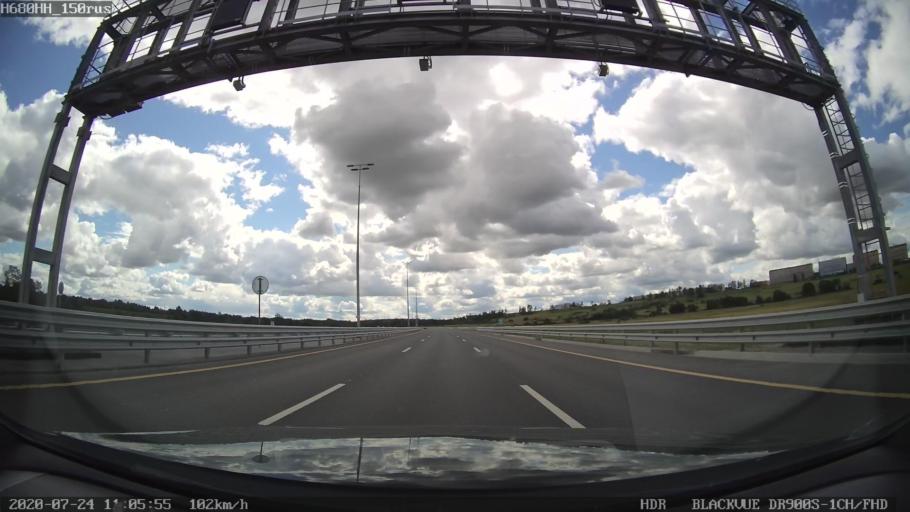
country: RU
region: St.-Petersburg
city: Shushary
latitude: 59.7705
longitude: 30.3641
